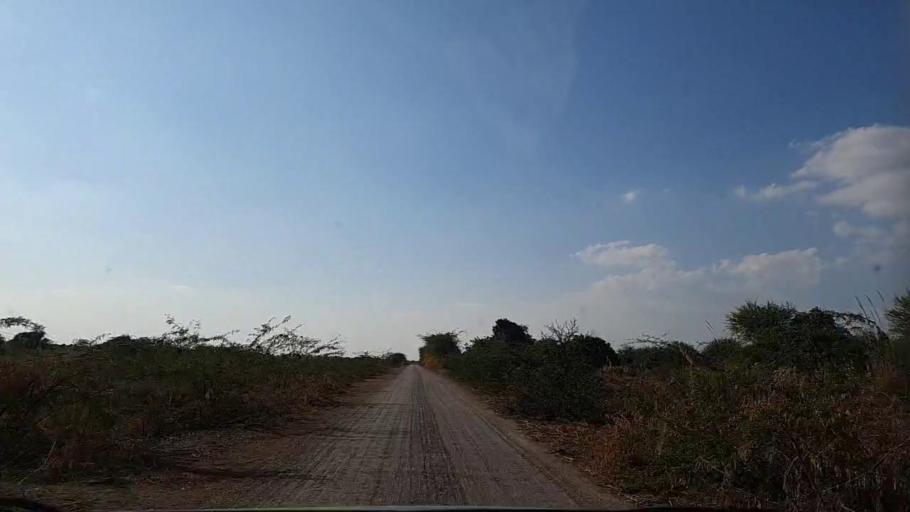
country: PK
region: Sindh
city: Pithoro
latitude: 25.6467
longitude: 69.3370
